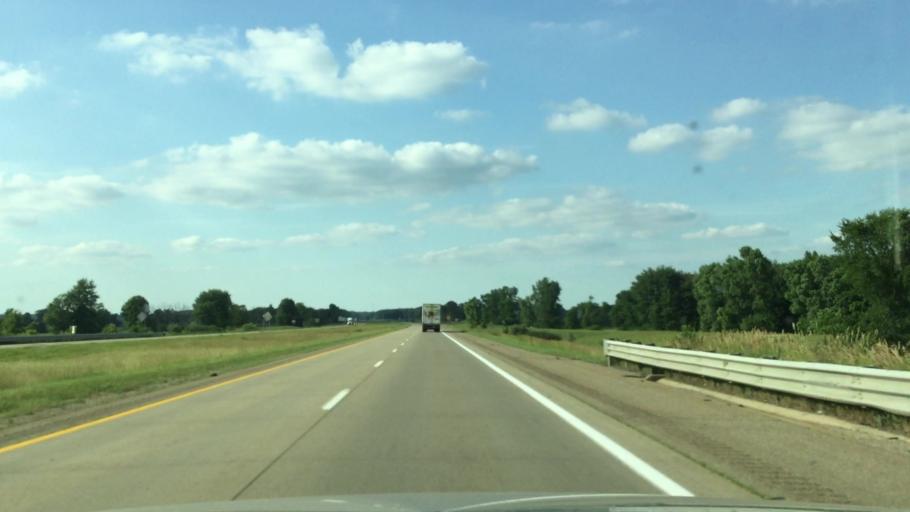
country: US
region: Michigan
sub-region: Branch County
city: Union City
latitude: 42.1067
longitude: -84.9958
